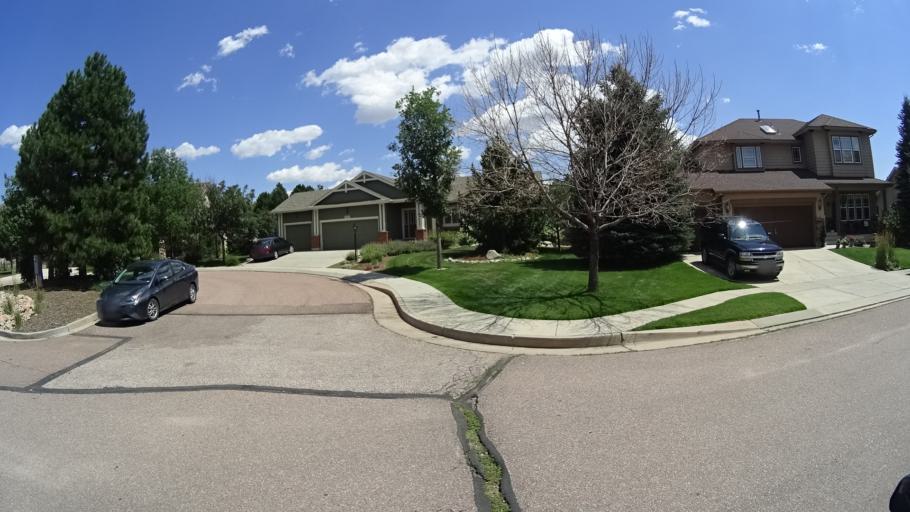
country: US
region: Colorado
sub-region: El Paso County
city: Black Forest
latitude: 38.9703
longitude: -104.7628
